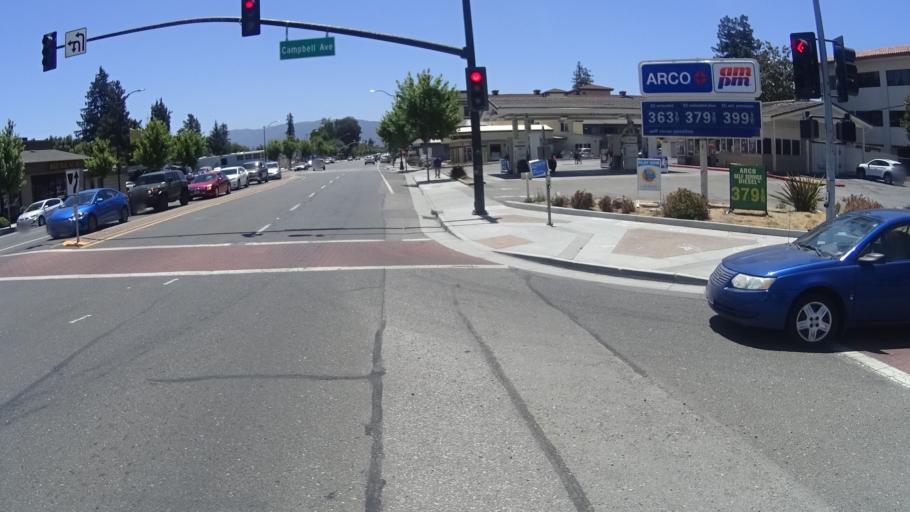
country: US
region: California
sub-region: Santa Clara County
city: Campbell
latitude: 37.2870
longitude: -121.9500
